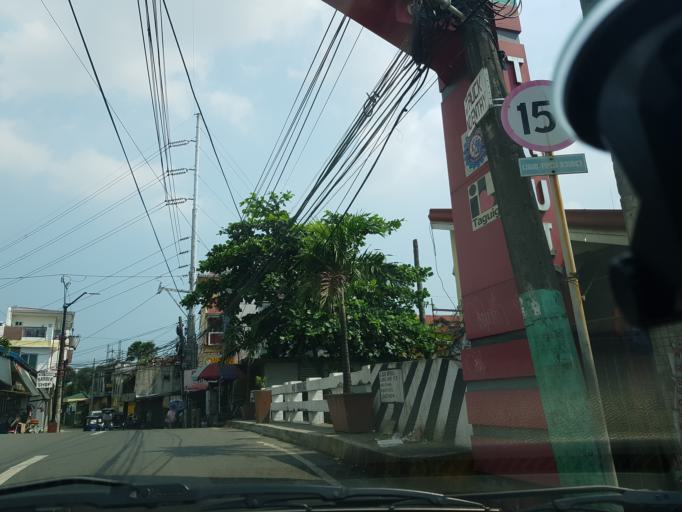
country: PH
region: Calabarzon
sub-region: Province of Rizal
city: Pateros
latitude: 14.5423
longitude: 121.0831
